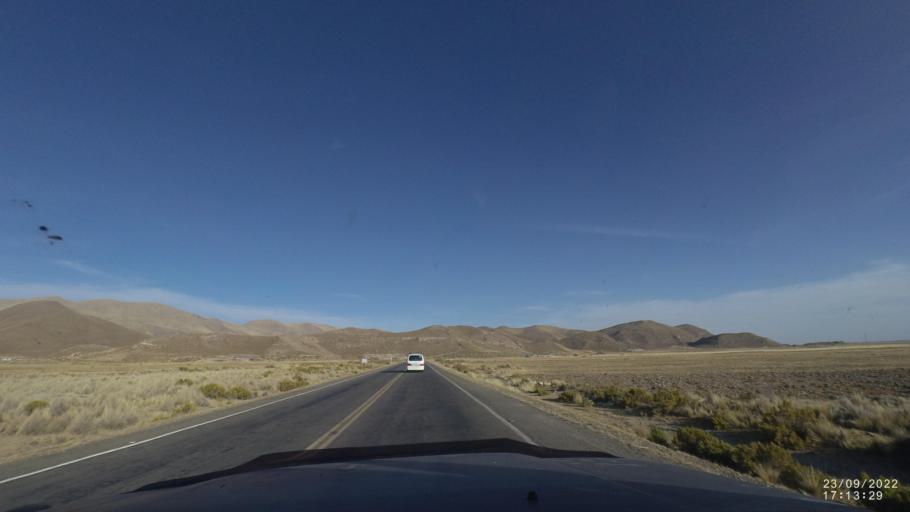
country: BO
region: Oruro
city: Totoral
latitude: -18.7113
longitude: -66.8745
